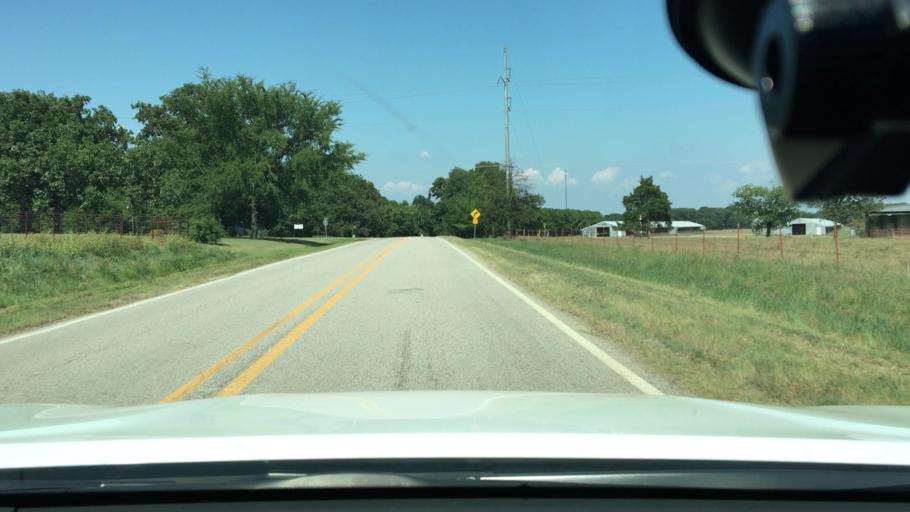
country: US
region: Arkansas
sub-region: Johnson County
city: Coal Hill
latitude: 35.3564
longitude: -93.5630
